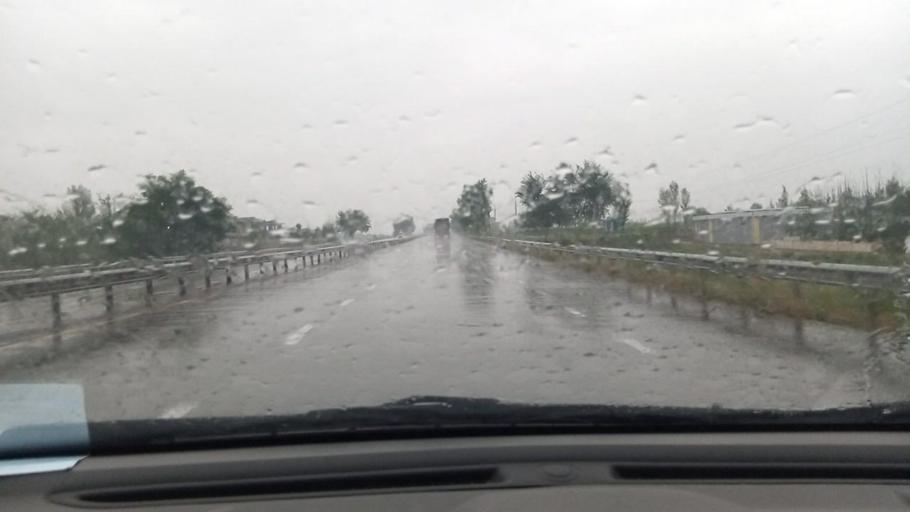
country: UZ
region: Toshkent Shahri
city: Bektemir
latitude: 41.1507
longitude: 69.4272
